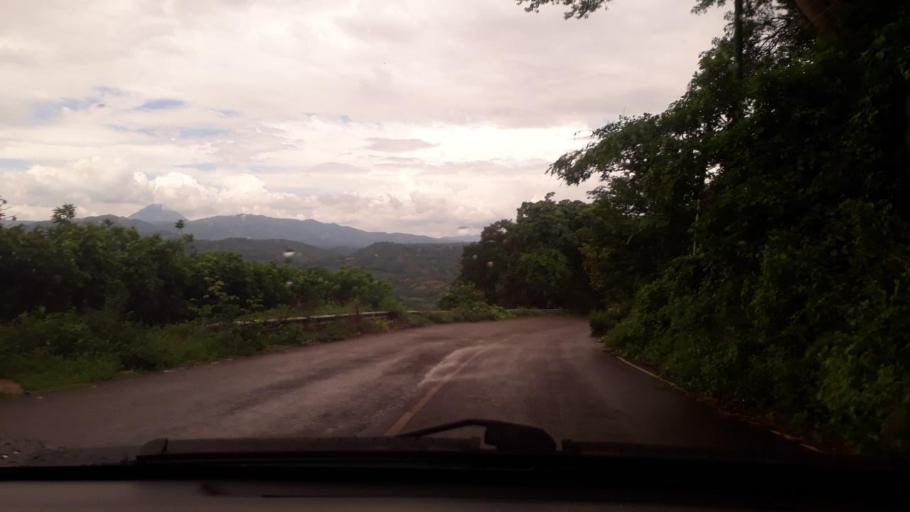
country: GT
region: Jutiapa
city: Comapa
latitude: 14.0328
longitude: -89.9104
